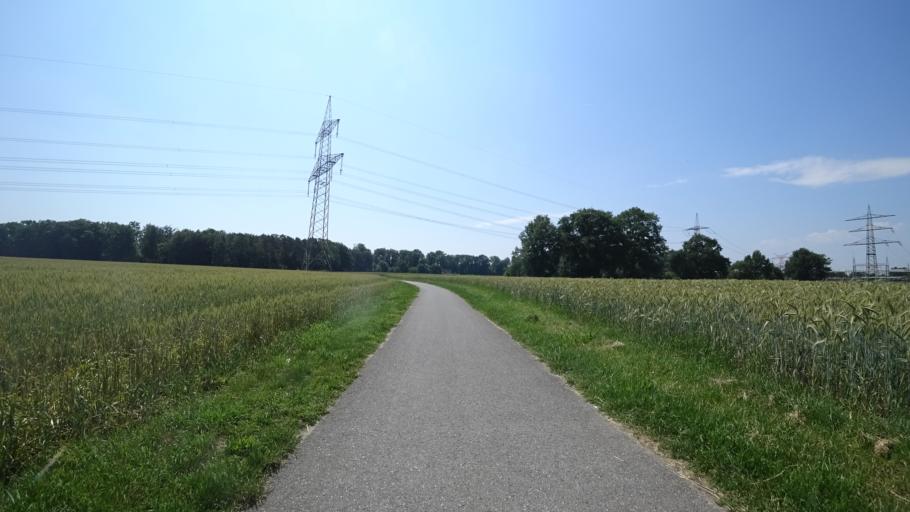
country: DE
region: North Rhine-Westphalia
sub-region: Regierungsbezirk Detmold
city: Guetersloh
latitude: 51.9295
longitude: 8.3688
